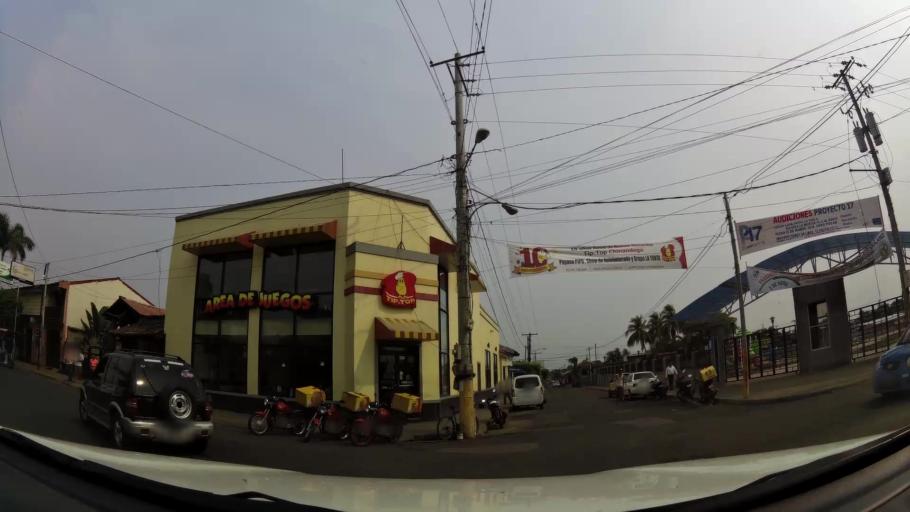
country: NI
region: Chinandega
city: Chinandega
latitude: 12.6308
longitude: -87.1352
